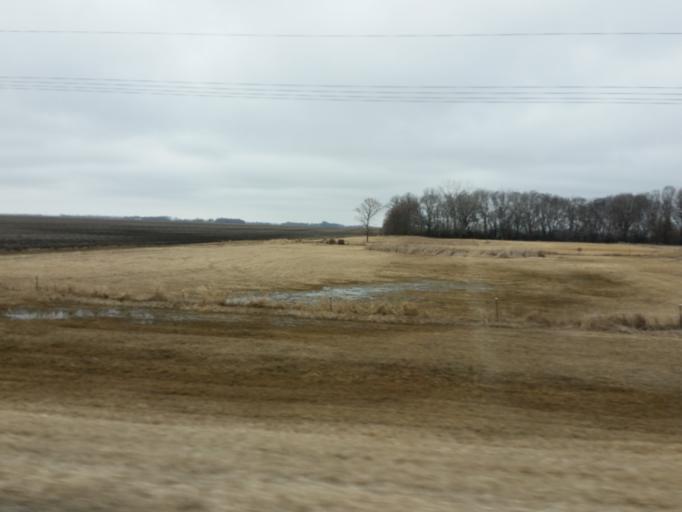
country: US
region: North Dakota
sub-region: Cass County
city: Casselton
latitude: 46.8380
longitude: -97.2215
